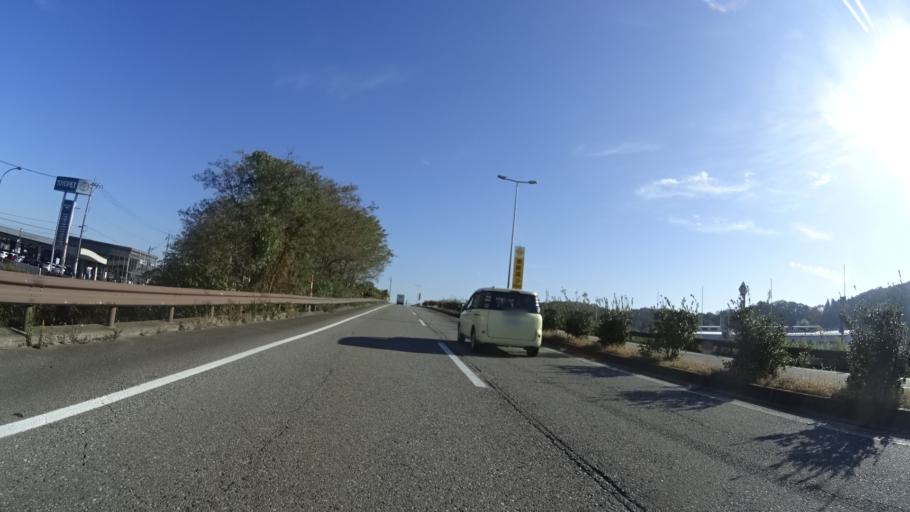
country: JP
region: Ishikawa
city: Komatsu
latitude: 36.3258
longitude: 136.4094
